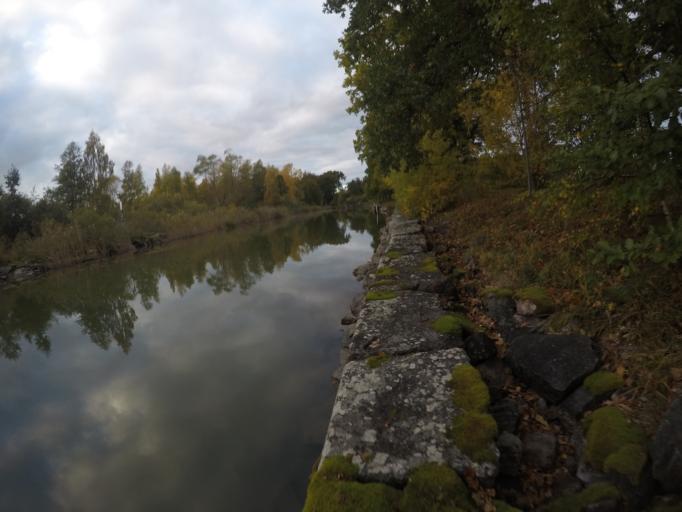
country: SE
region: Vaestmanland
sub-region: Arboga Kommun
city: Tyringe
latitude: 59.2919
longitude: 16.0030
